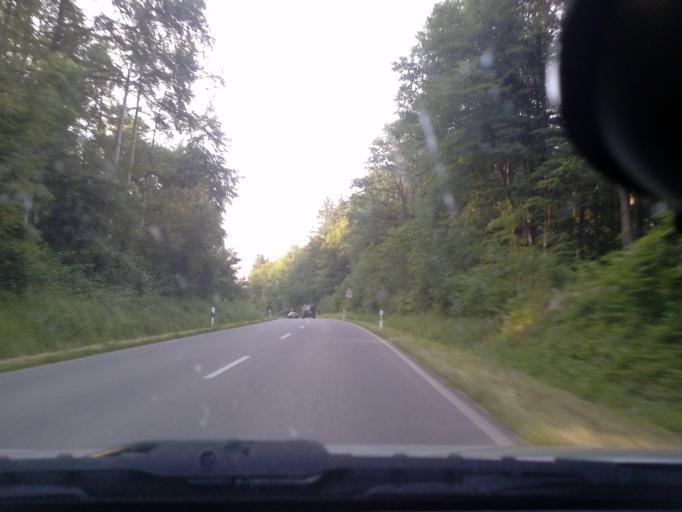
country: DE
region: Baden-Wuerttemberg
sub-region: Karlsruhe Region
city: Woessingen
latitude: 48.9975
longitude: 8.6333
